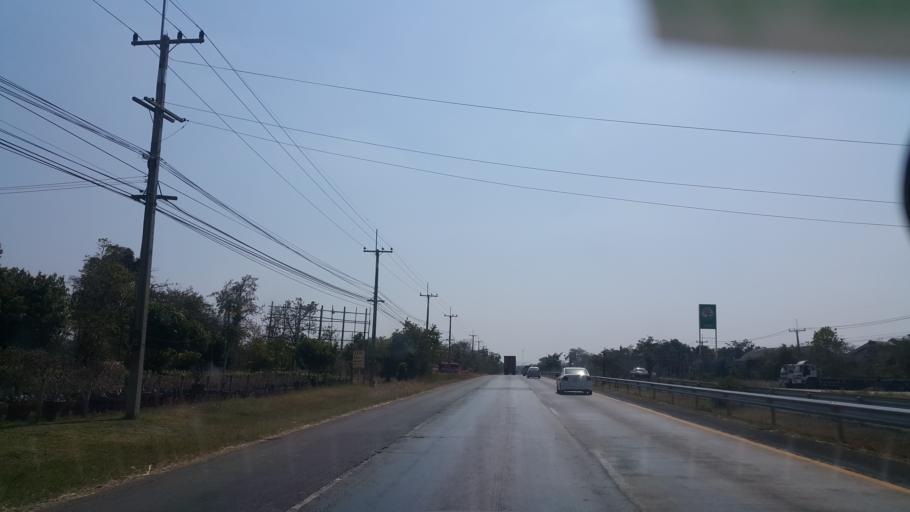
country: TH
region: Nakhon Ratchasima
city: Sida
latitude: 15.5332
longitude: 102.5447
